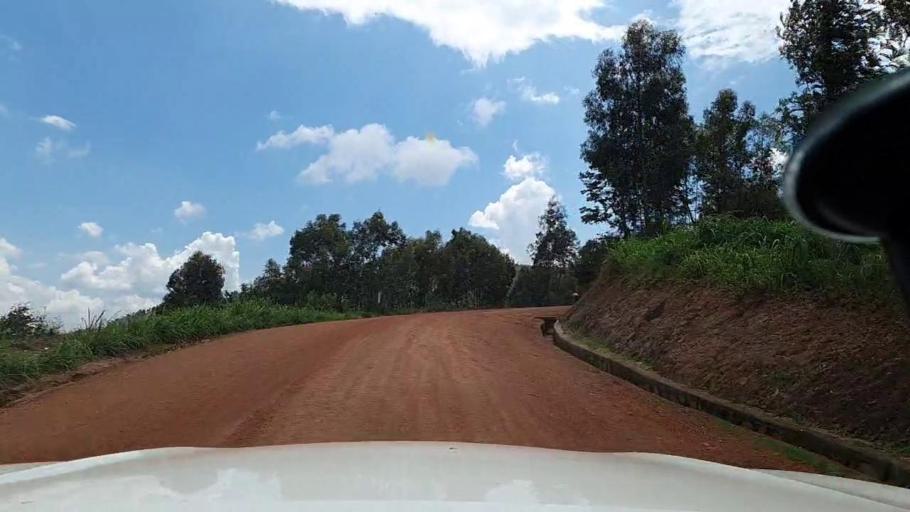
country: RW
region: Kigali
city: Kigali
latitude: -1.7742
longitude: 29.8419
